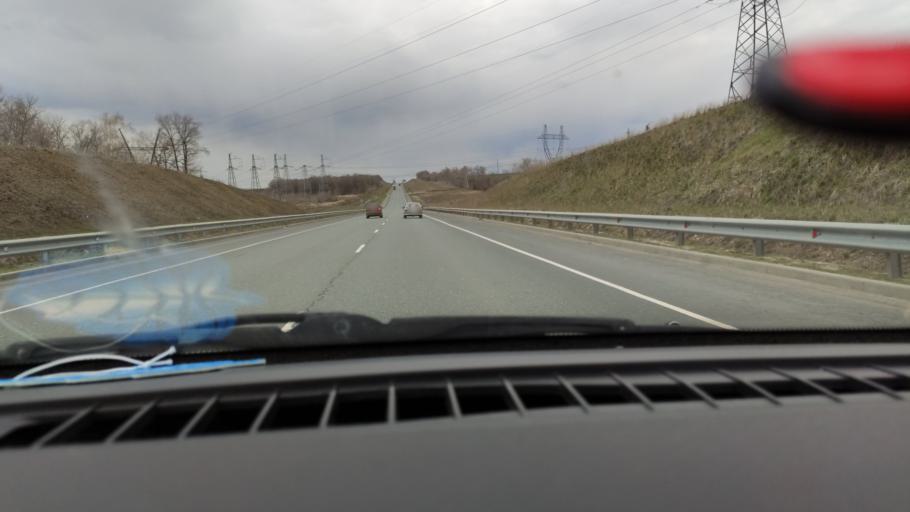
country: RU
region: Saratov
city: Yelshanka
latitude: 51.8233
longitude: 46.3147
